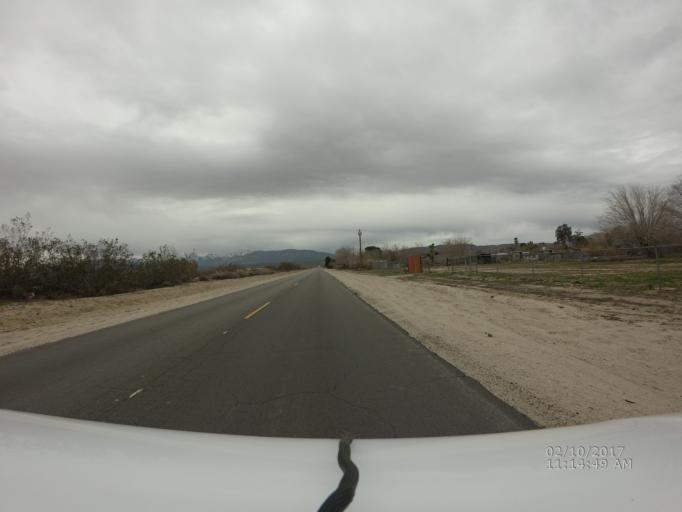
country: US
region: California
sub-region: Los Angeles County
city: Littlerock
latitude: 34.5389
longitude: -117.9581
